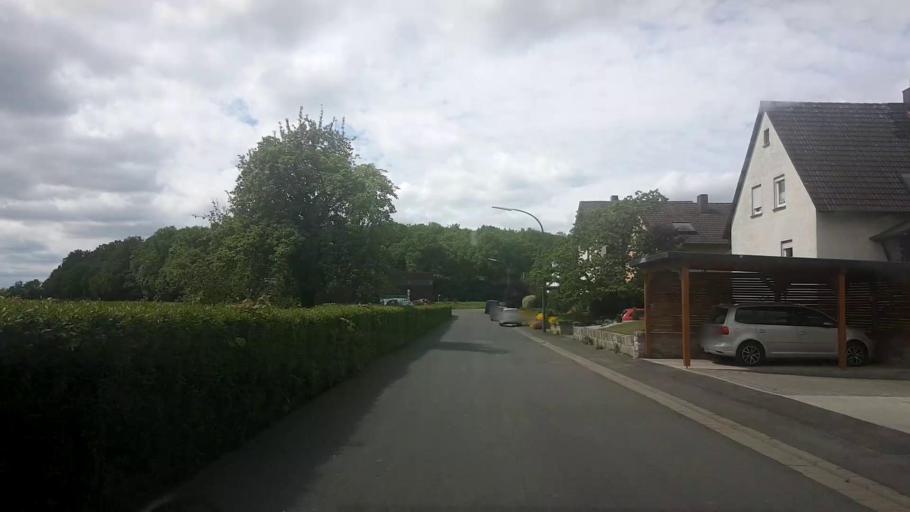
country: DE
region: Bavaria
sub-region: Upper Franconia
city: Bad Staffelstein
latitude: 50.1337
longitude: 11.0225
